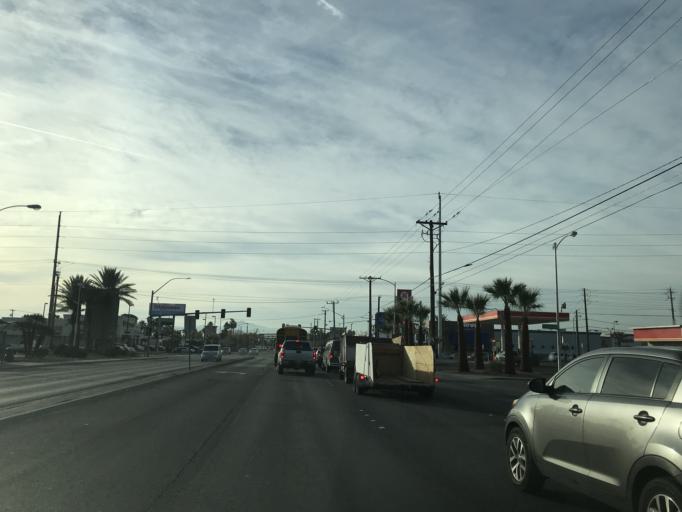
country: US
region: Nevada
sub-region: Clark County
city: Winchester
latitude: 36.1453
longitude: -115.0655
